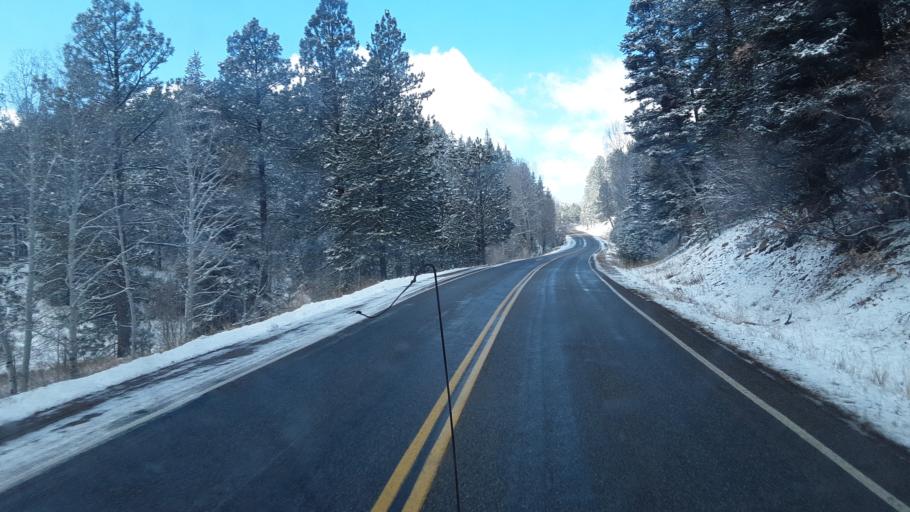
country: US
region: Colorado
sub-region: La Plata County
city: Bayfield
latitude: 37.3524
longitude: -107.6506
